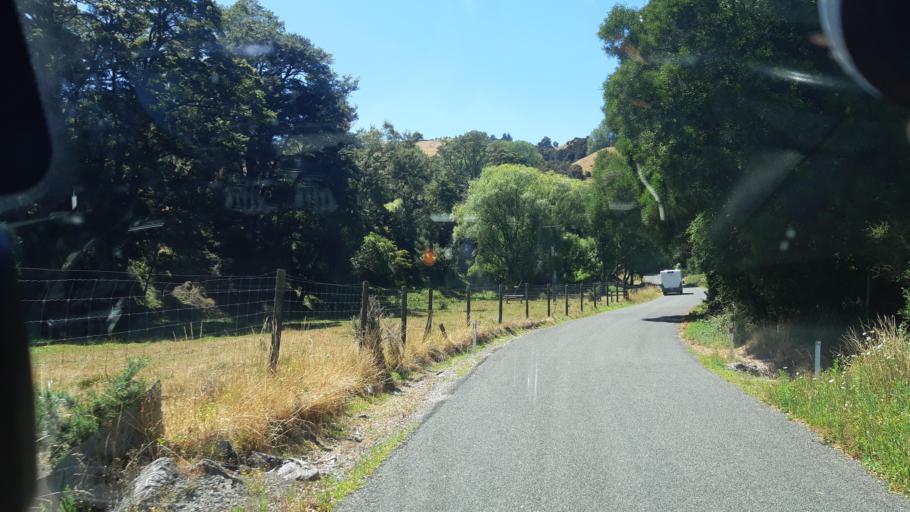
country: NZ
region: Tasman
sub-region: Tasman District
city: Motueka
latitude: -41.0429
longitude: 172.9167
